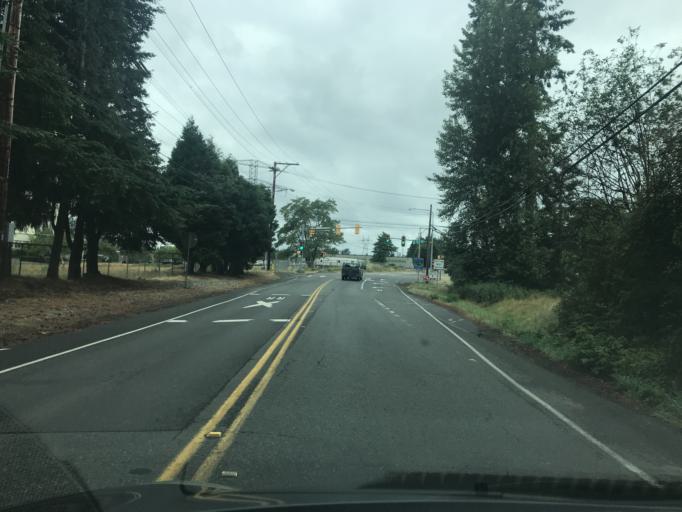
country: US
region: Washington
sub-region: King County
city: Covington
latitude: 47.3491
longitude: -122.1171
